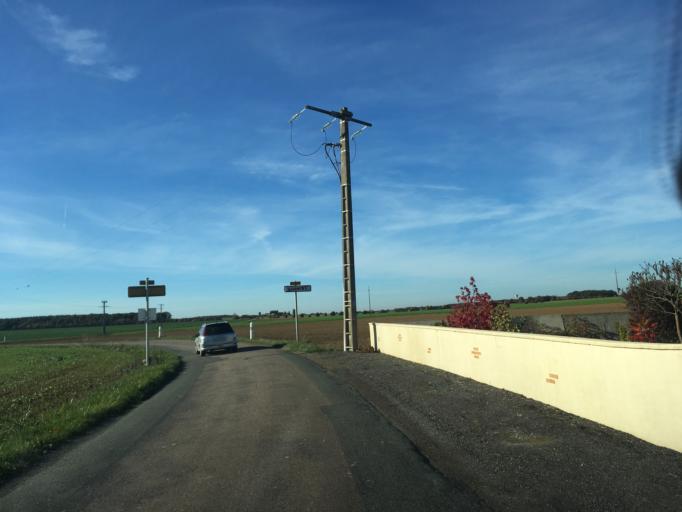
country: FR
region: Haute-Normandie
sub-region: Departement de l'Eure
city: Pacy-sur-Eure
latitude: 49.0403
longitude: 1.4224
